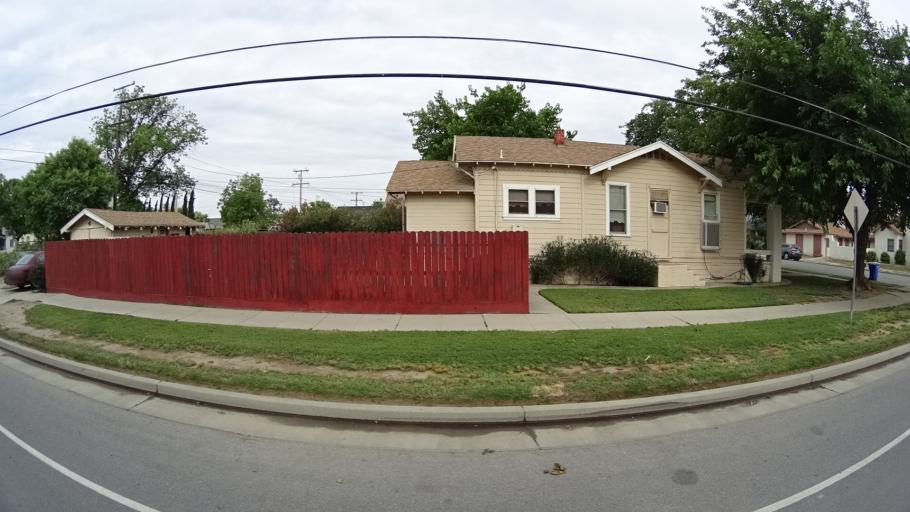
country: US
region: California
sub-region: Kings County
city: Hanford
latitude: 36.3328
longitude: -119.6494
